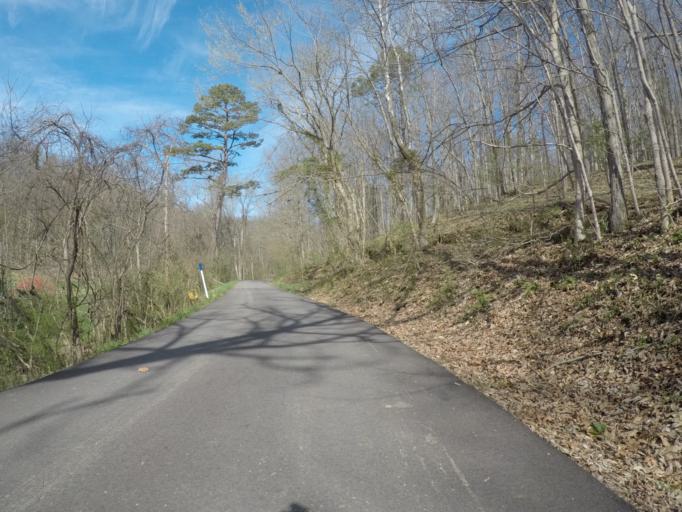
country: US
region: West Virginia
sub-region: Cabell County
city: Pea Ridge
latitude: 38.3929
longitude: -82.3489
